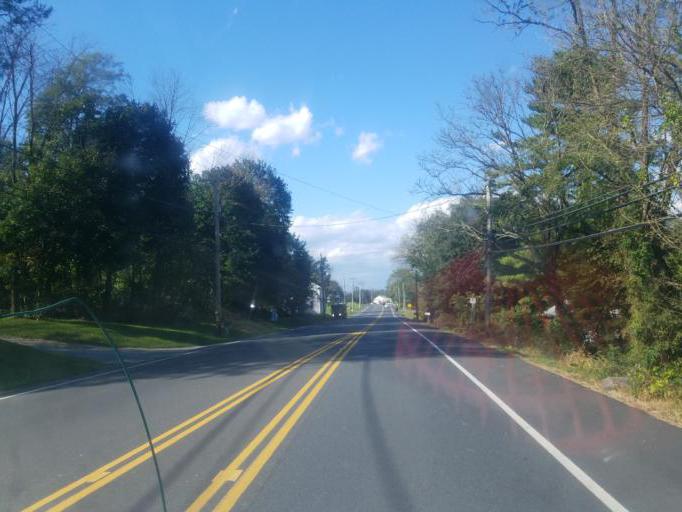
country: US
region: Pennsylvania
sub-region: Dauphin County
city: Middletown
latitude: 40.1941
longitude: -76.6932
